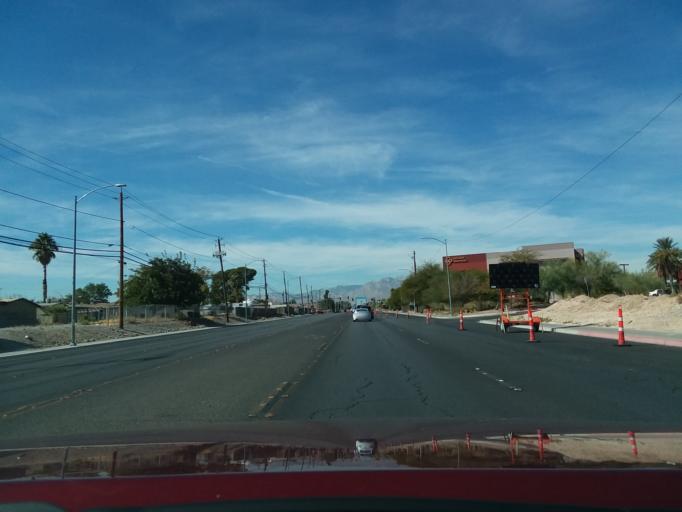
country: US
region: Nevada
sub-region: Clark County
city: Las Vegas
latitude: 36.1958
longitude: -115.1489
